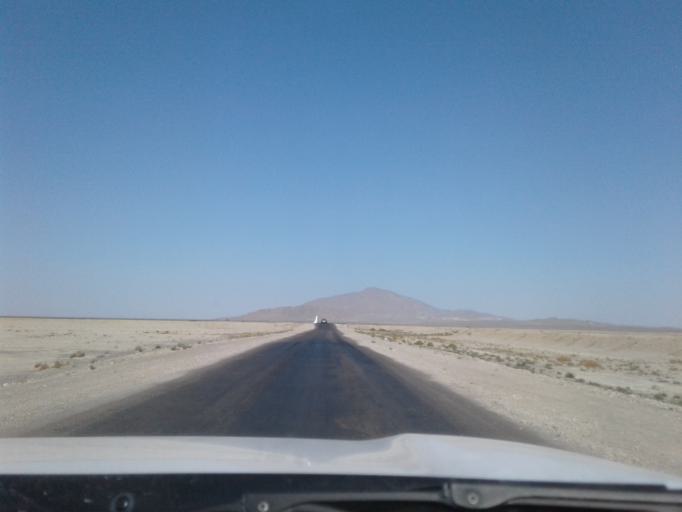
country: TM
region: Balkan
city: Gumdag
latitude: 39.2389
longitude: 54.7037
